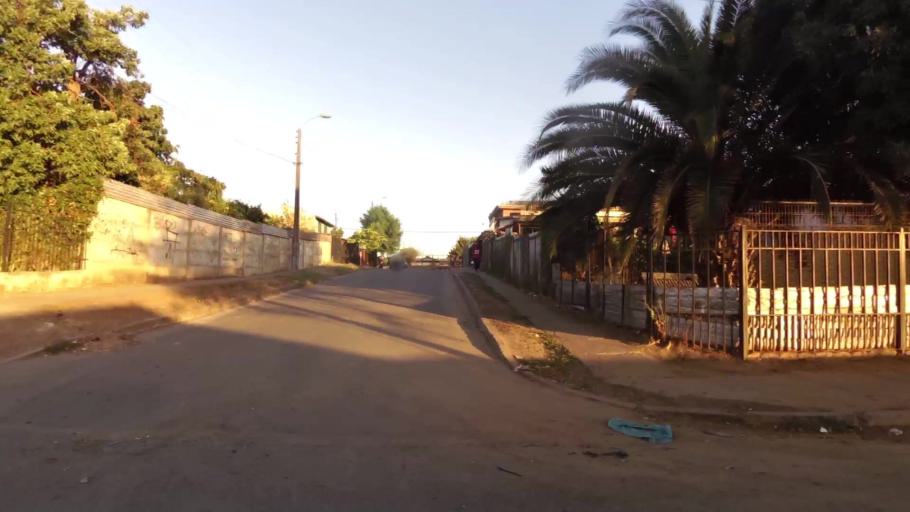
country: CL
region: Maule
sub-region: Provincia de Talca
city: Talca
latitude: -35.4442
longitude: -71.6367
